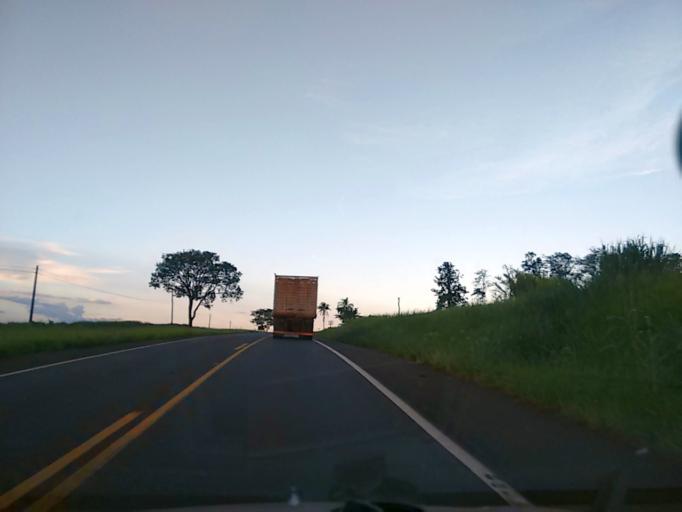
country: BR
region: Sao Paulo
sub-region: Boa Esperanca Do Sul
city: Boa Esperanca do Sul
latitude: -22.1289
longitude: -48.4591
